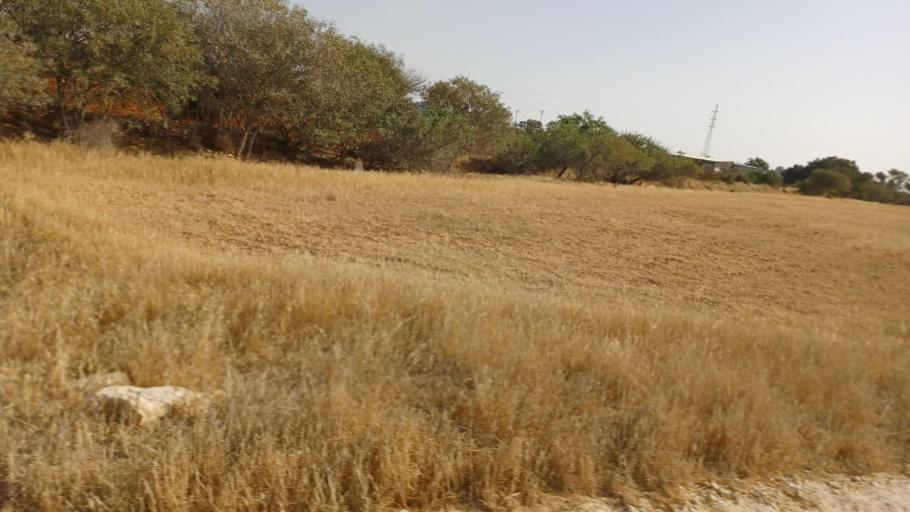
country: CY
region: Ammochostos
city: Liopetri
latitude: 34.9947
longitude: 33.8927
